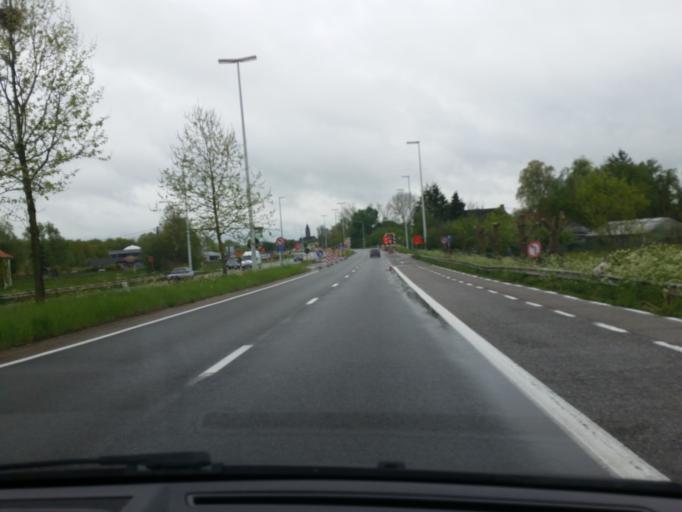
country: BE
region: Flanders
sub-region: Provincie Antwerpen
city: Lier
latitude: 51.1319
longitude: 4.5495
